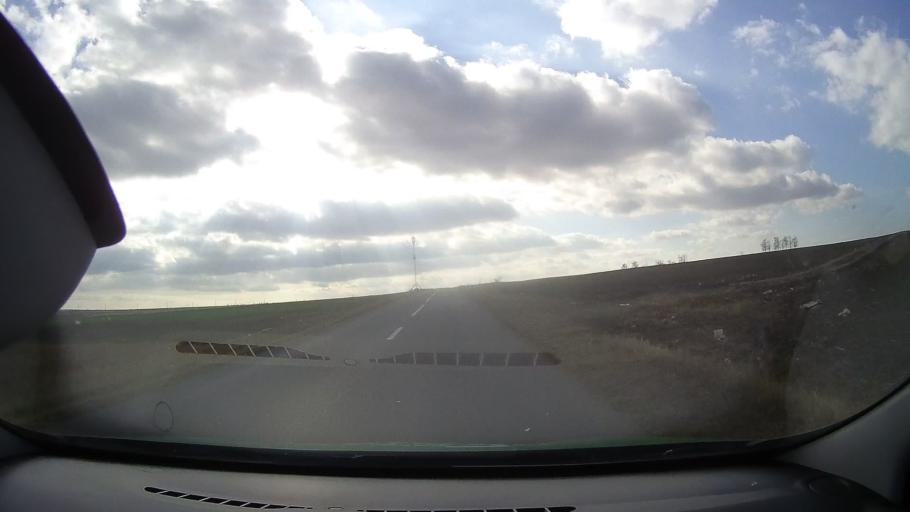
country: RO
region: Constanta
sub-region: Comuna Sacele
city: Sacele
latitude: 44.4942
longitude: 28.6559
